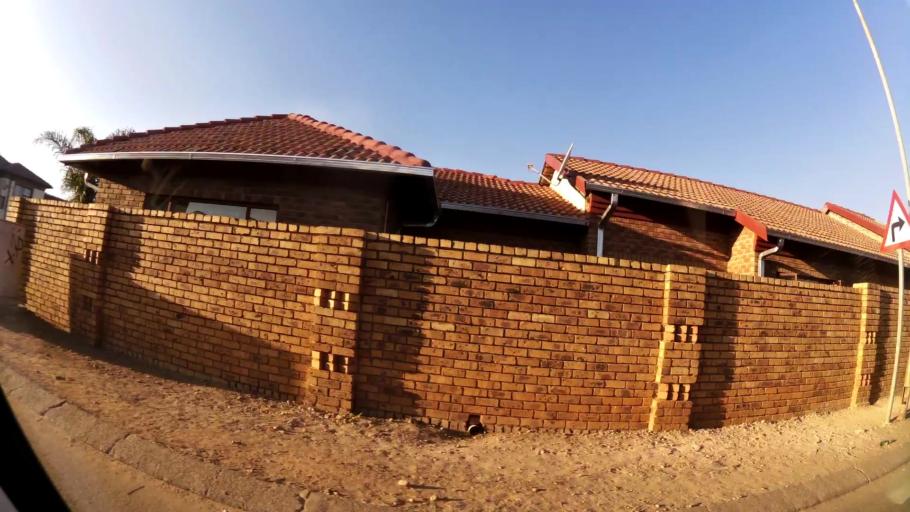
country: ZA
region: Gauteng
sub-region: City of Tshwane Metropolitan Municipality
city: Cullinan
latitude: -25.7237
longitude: 28.3947
